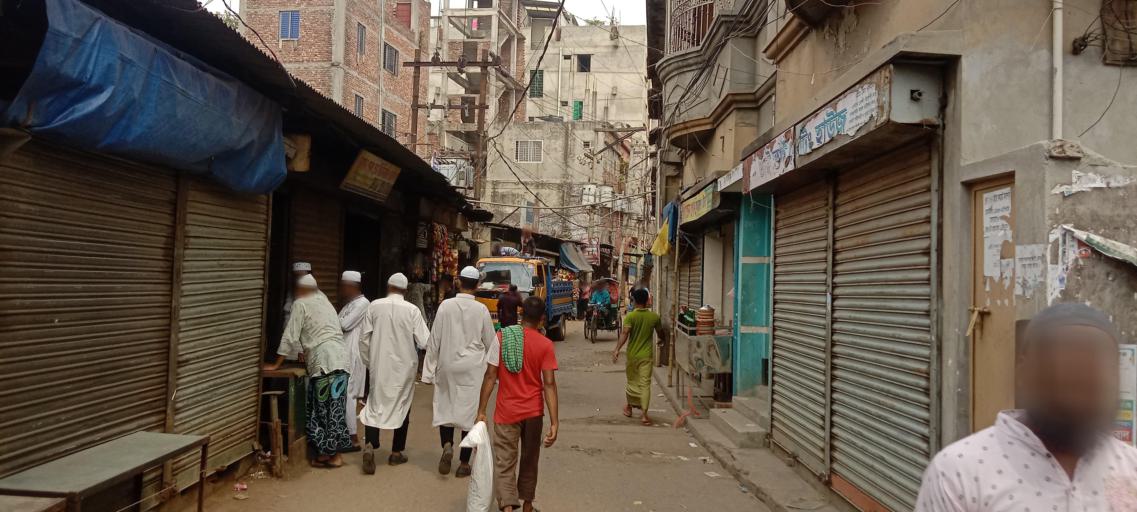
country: BD
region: Dhaka
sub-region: Dhaka
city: Dhaka
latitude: 23.7086
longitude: 90.3969
